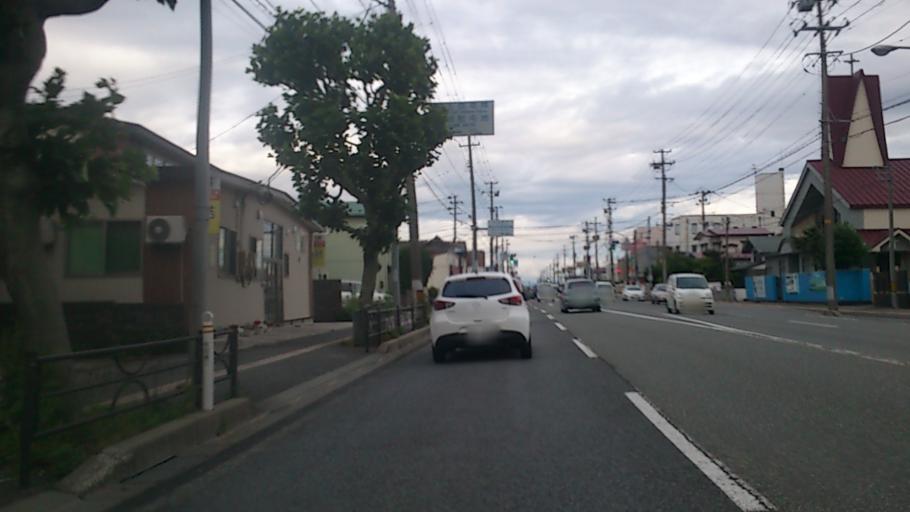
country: JP
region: Akita
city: Akita Shi
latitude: 39.7479
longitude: 140.0785
